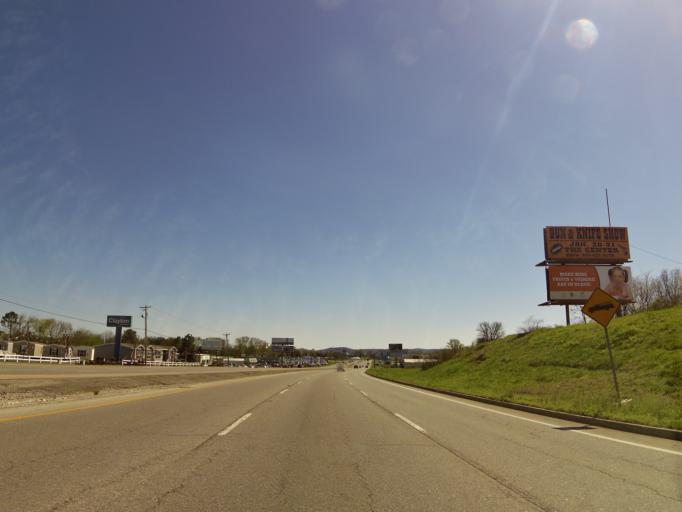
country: US
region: Kentucky
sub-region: Pulaski County
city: Somerset
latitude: 37.0259
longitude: -84.6264
